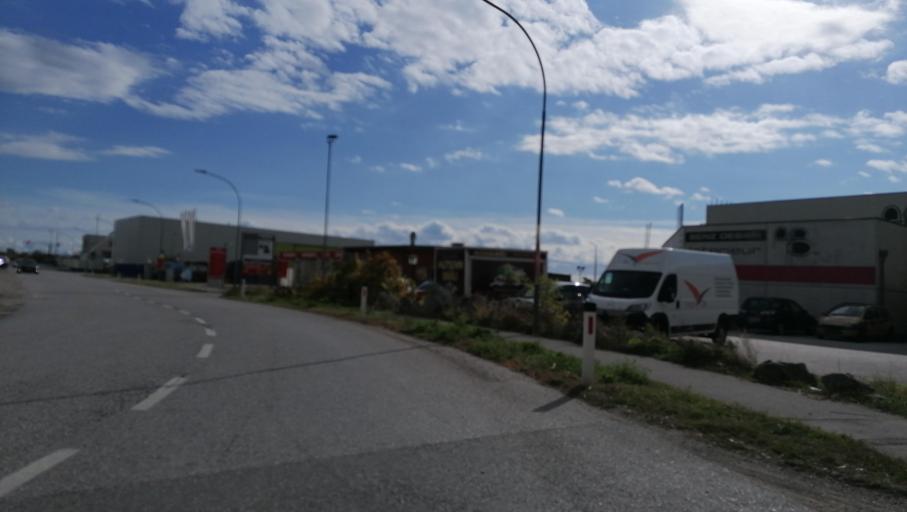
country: AT
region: Lower Austria
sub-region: Politischer Bezirk Baden
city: Teesdorf
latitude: 47.9754
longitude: 16.2786
